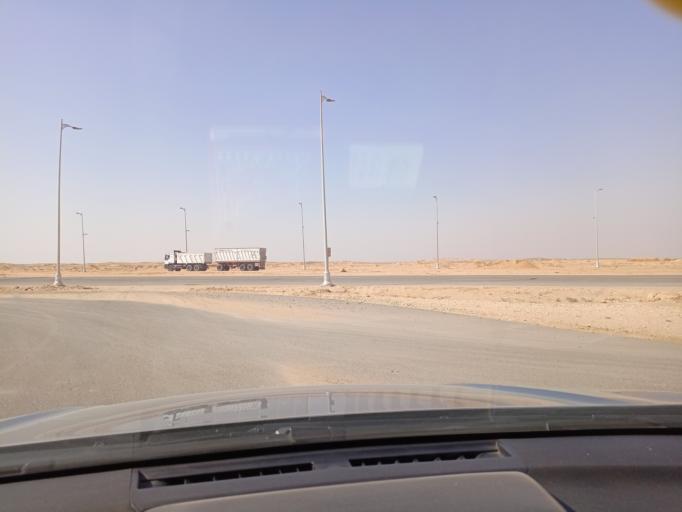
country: EG
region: Muhafazat al Qalyubiyah
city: Al Khankah
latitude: 30.0437
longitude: 31.7130
